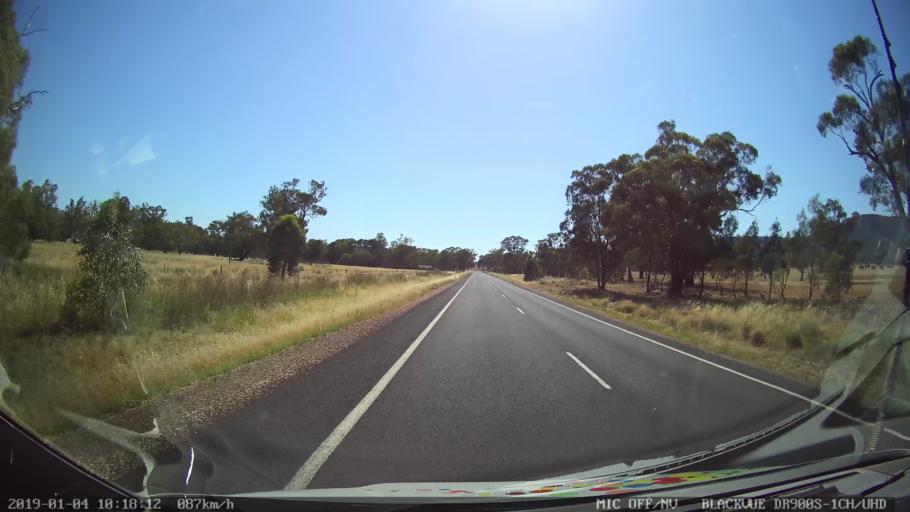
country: AU
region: New South Wales
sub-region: Cabonne
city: Canowindra
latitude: -33.3828
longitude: 148.4629
